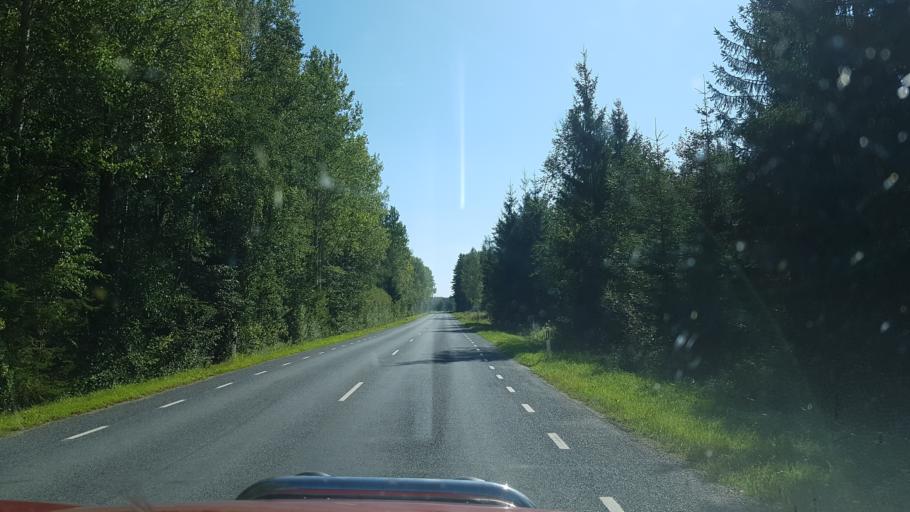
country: EE
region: Polvamaa
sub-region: Polva linn
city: Polva
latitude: 58.2746
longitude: 27.1161
